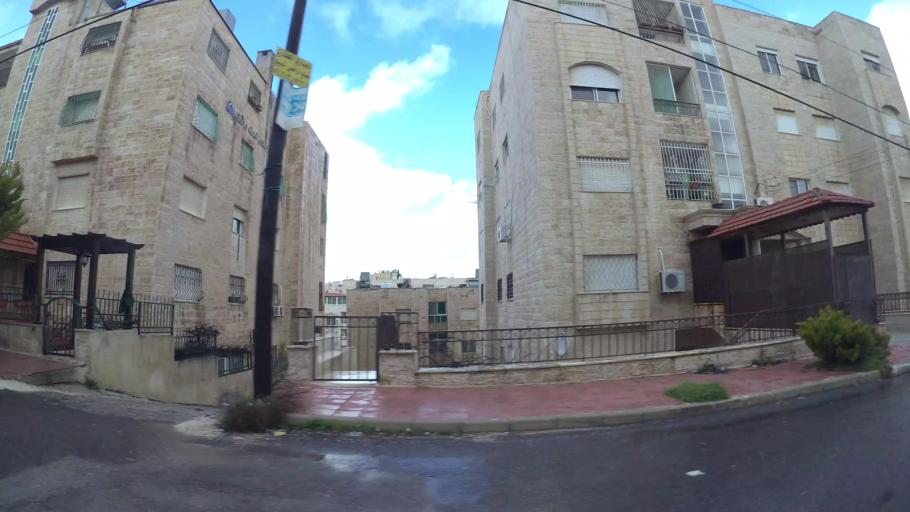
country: JO
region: Amman
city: Al Jubayhah
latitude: 32.0320
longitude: 35.8690
